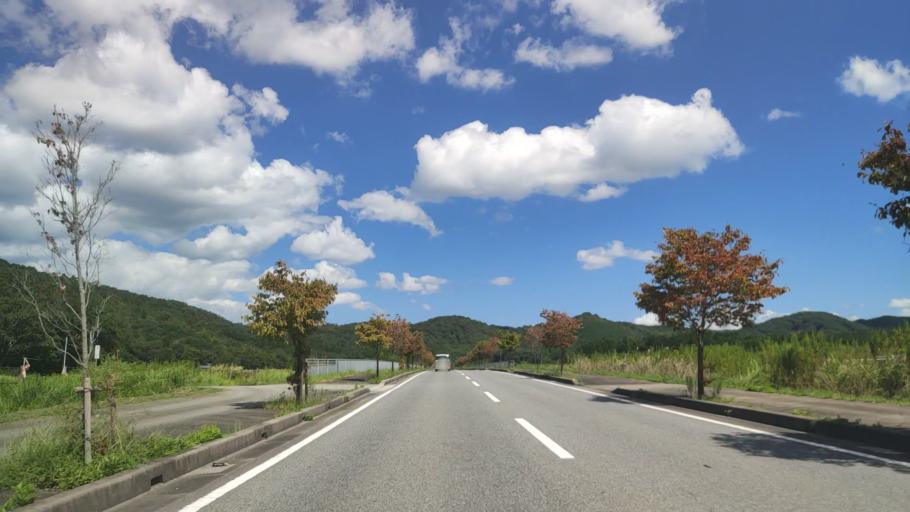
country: JP
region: Kyoto
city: Fukuchiyama
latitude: 35.2532
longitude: 135.1410
